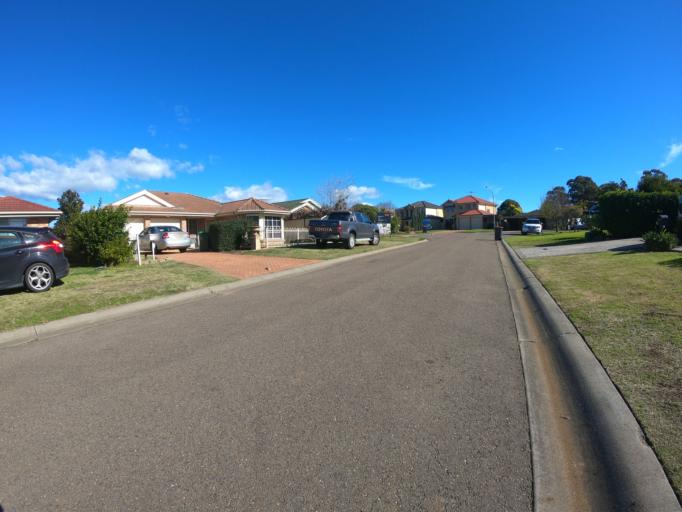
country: AU
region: New South Wales
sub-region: Hawkesbury
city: South Windsor
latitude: -33.6287
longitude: 150.8035
